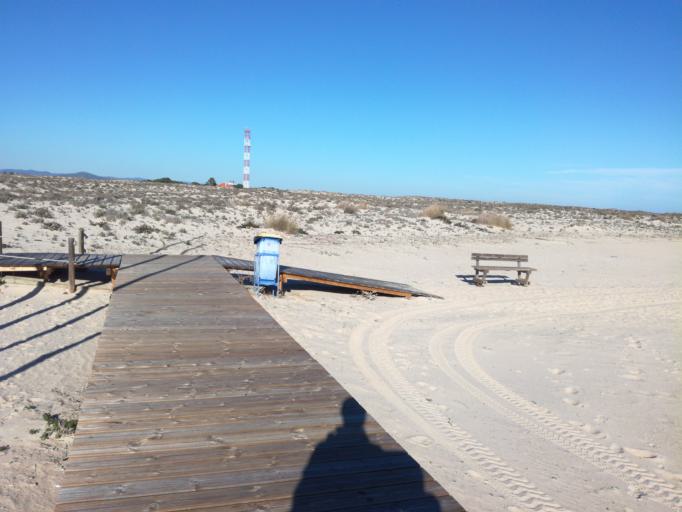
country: PT
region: Faro
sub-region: Olhao
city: Olhao
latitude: 37.0140
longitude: -7.7961
